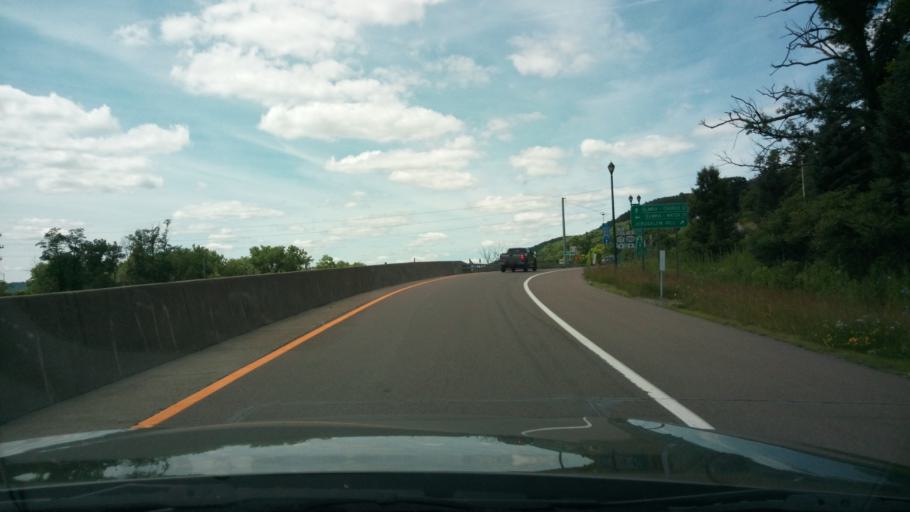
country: US
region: New York
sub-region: Chemung County
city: Elmira
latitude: 42.0895
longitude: -76.7817
